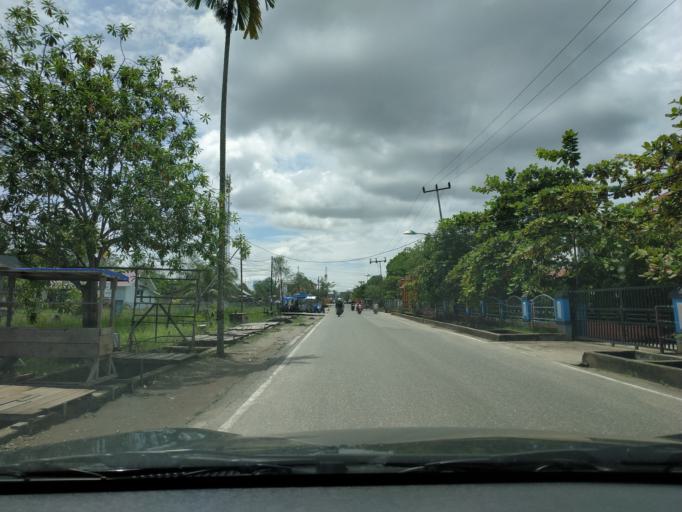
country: ID
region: Riau
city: Tembilahan
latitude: -0.3192
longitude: 103.1650
